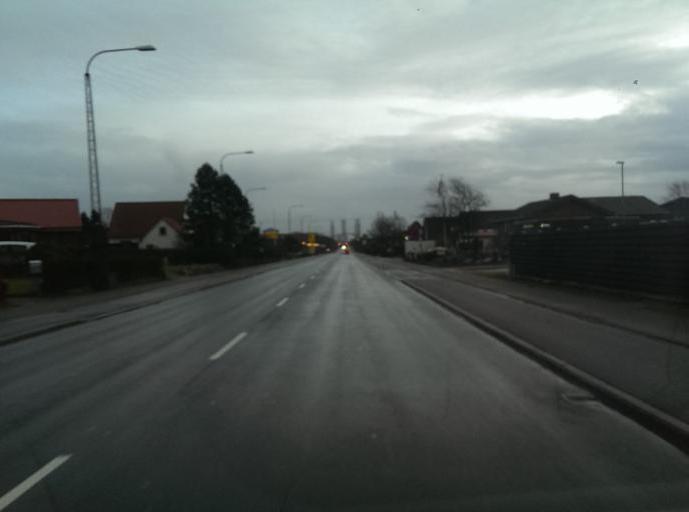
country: DK
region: South Denmark
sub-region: Esbjerg Kommune
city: Esbjerg
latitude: 55.4962
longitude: 8.4090
